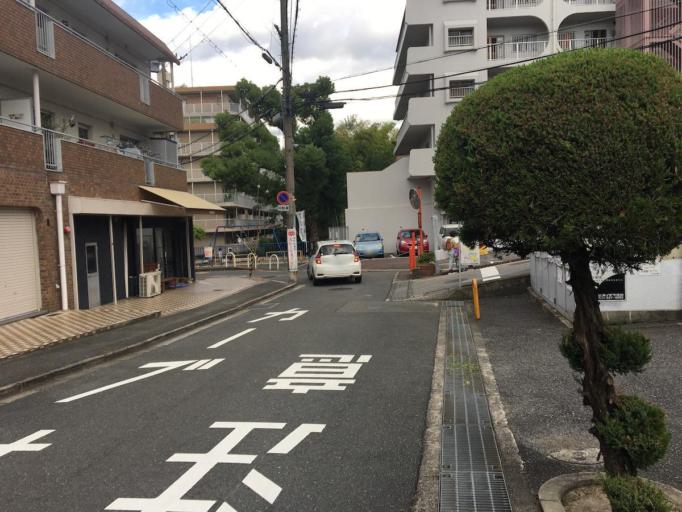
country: JP
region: Osaka
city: Suita
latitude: 34.7993
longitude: 135.5207
